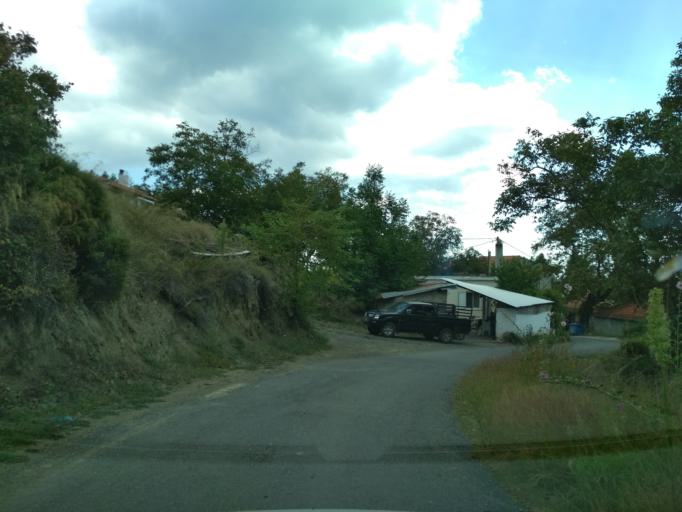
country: GR
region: Central Greece
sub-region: Nomos Evvoias
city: Roviai
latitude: 38.8496
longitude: 23.2892
